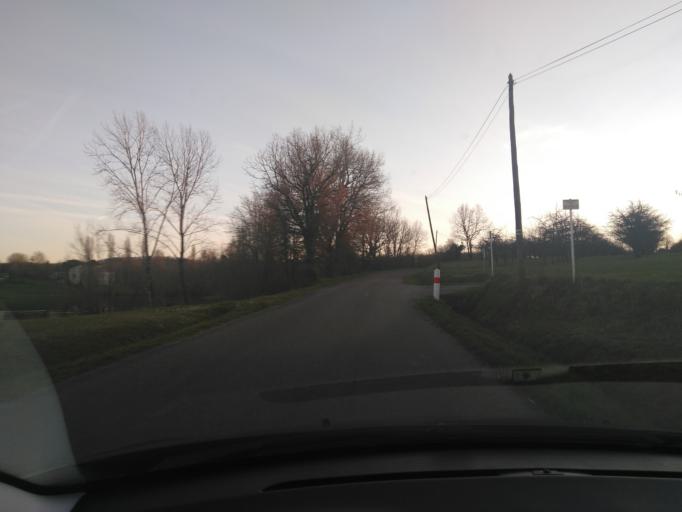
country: FR
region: Aquitaine
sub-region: Departement du Lot-et-Garonne
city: Saint-Hilaire
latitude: 44.5382
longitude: 0.6980
